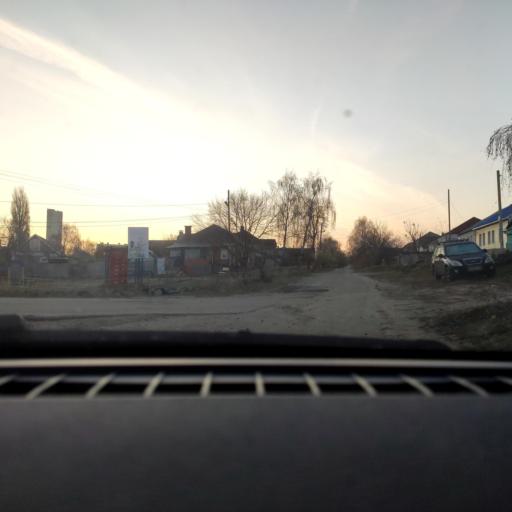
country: RU
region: Voronezj
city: Voronezh
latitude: 51.7051
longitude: 39.2650
